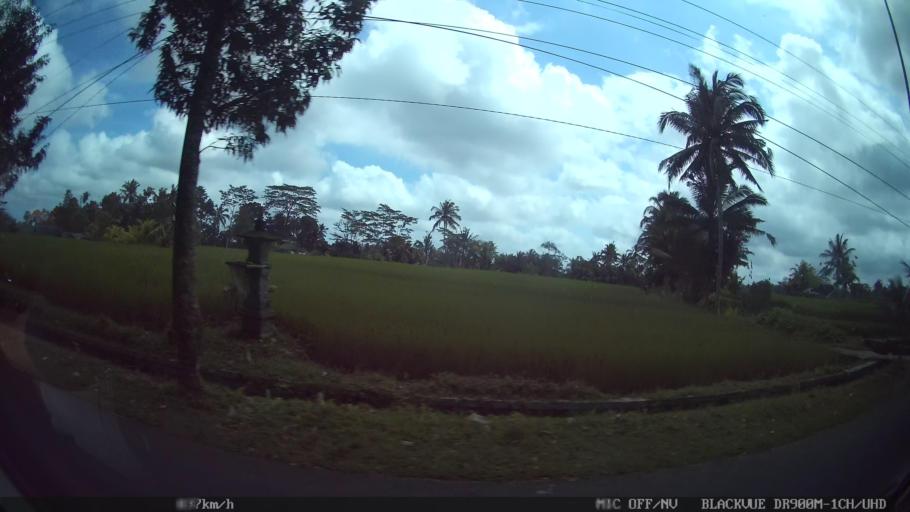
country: ID
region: Bali
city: Banjar Madangan Kaja
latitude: -8.4719
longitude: 115.3238
